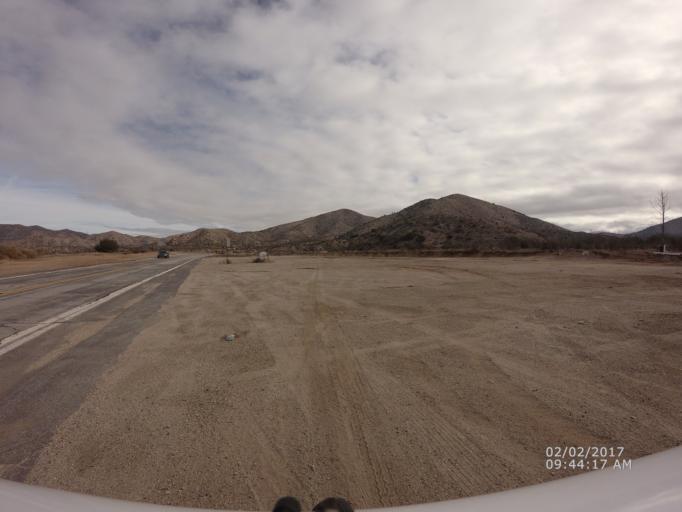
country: US
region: California
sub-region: Los Angeles County
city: Vincent
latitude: 34.4467
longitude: -118.1018
